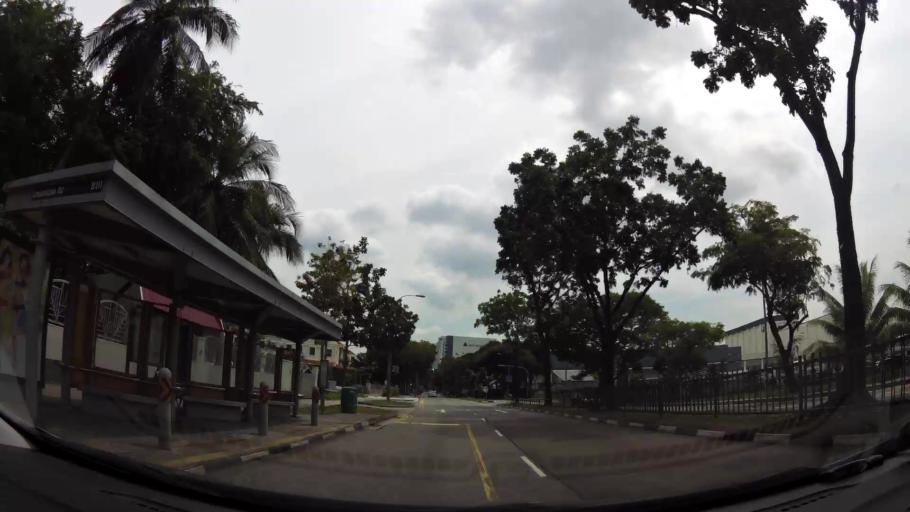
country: MY
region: Johor
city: Johor Bahru
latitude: 1.3401
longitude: 103.7162
